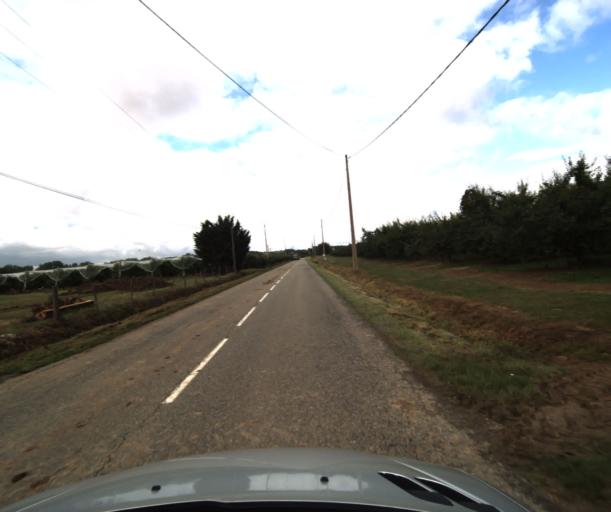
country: FR
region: Midi-Pyrenees
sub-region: Departement du Tarn-et-Garonne
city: Saint-Nicolas-de-la-Grave
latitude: 44.0241
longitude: 1.0216
